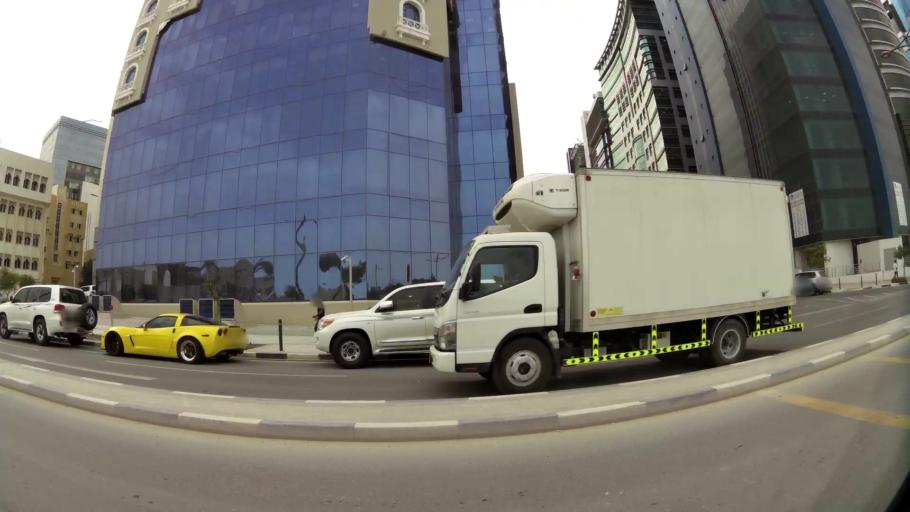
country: QA
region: Baladiyat ad Dawhah
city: Doha
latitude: 25.2884
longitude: 51.5474
